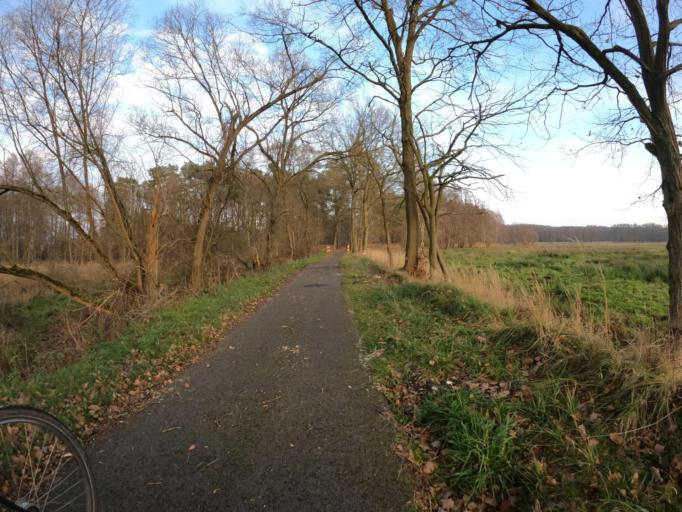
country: PL
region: West Pomeranian Voivodeship
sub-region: Powiat policki
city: Nowe Warpno
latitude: 53.6900
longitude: 14.2840
